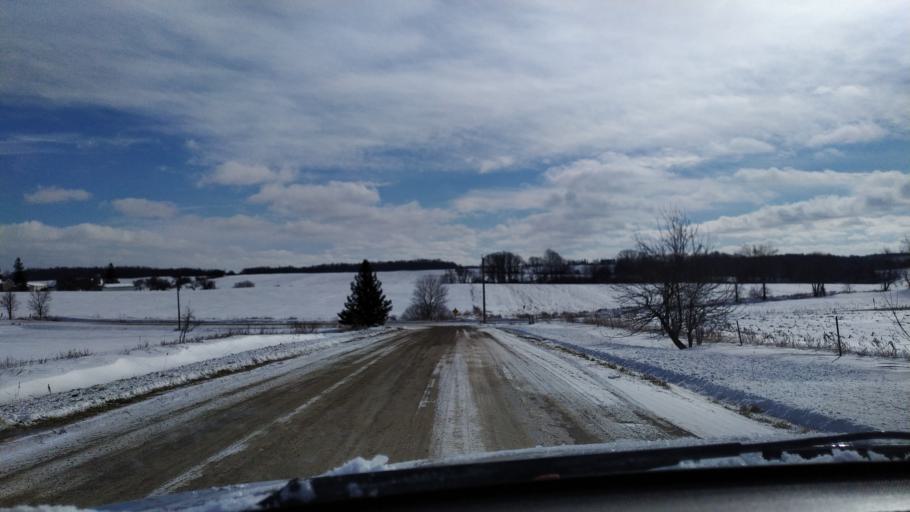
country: CA
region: Ontario
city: Waterloo
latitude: 43.4698
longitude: -80.7383
